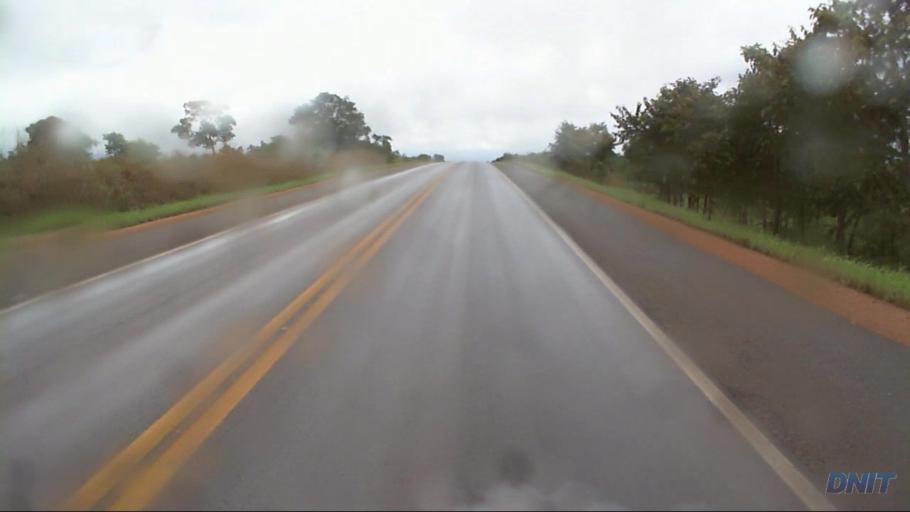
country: BR
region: Goias
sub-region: Padre Bernardo
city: Padre Bernardo
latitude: -15.1997
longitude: -48.4511
